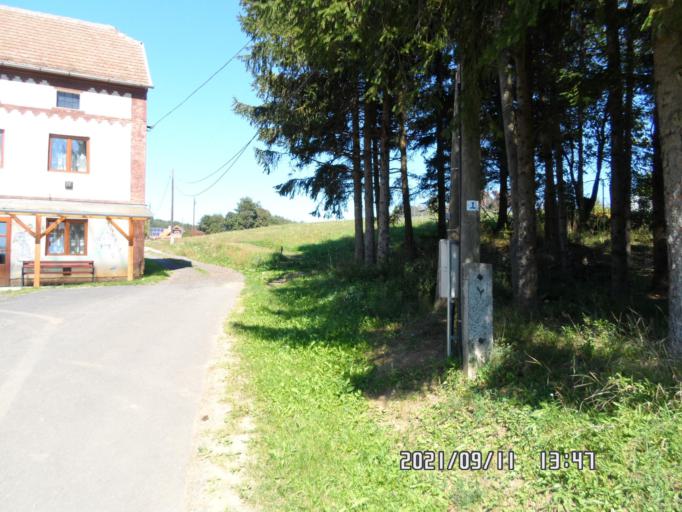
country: HU
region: Zala
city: Zalalovo
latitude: 46.7740
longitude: 16.6972
